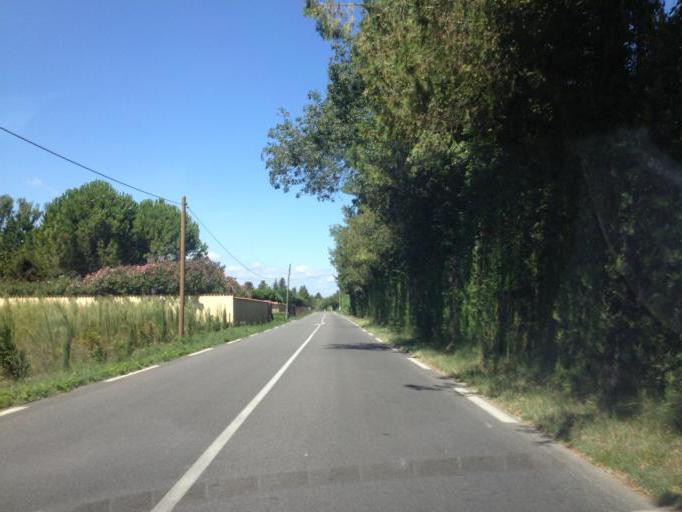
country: FR
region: Languedoc-Roussillon
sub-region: Departement du Gard
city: Sauveterre
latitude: 44.0066
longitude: 4.8105
